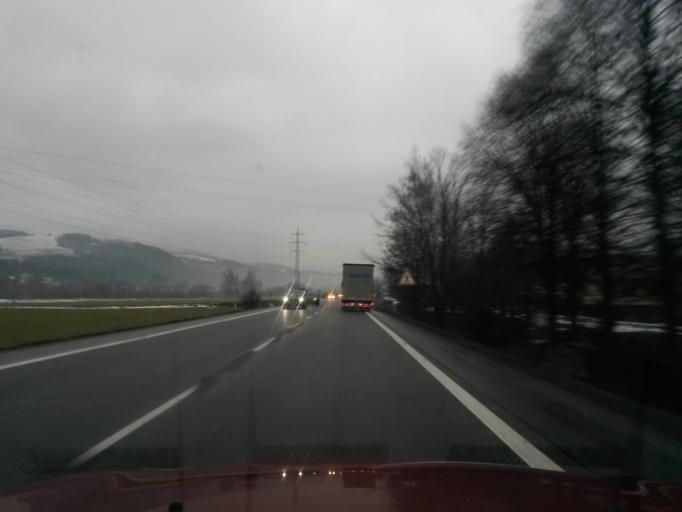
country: SK
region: Zilinsky
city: Kysucke Nove Mesto
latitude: 49.3362
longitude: 18.8084
